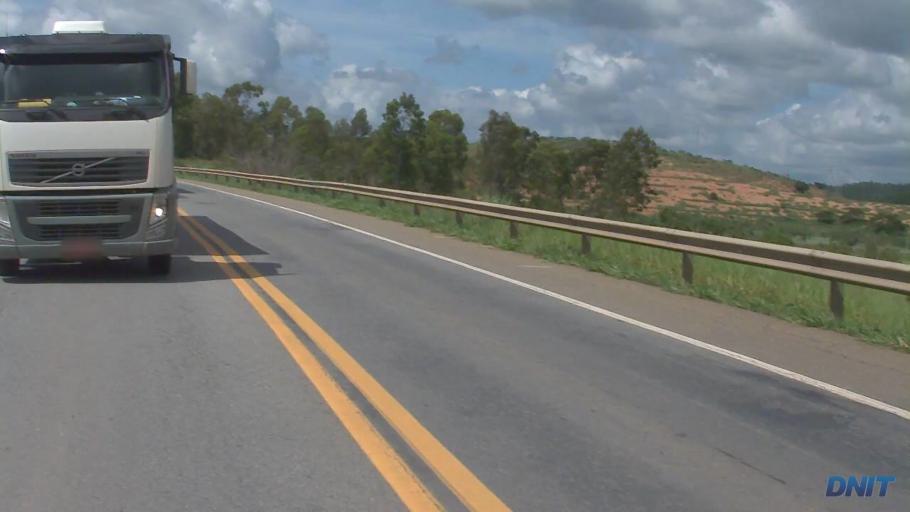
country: BR
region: Minas Gerais
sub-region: Governador Valadares
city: Governador Valadares
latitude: -19.0631
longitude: -42.1629
